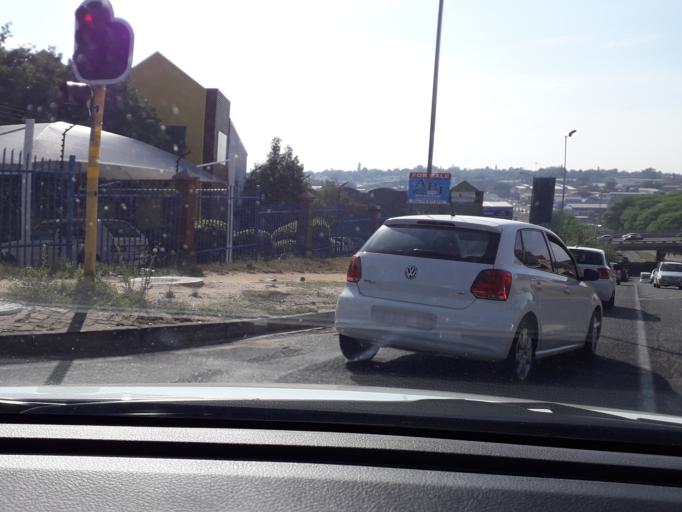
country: ZA
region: Gauteng
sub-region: City of Johannesburg Metropolitan Municipality
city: Roodepoort
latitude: -26.0782
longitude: 27.9689
